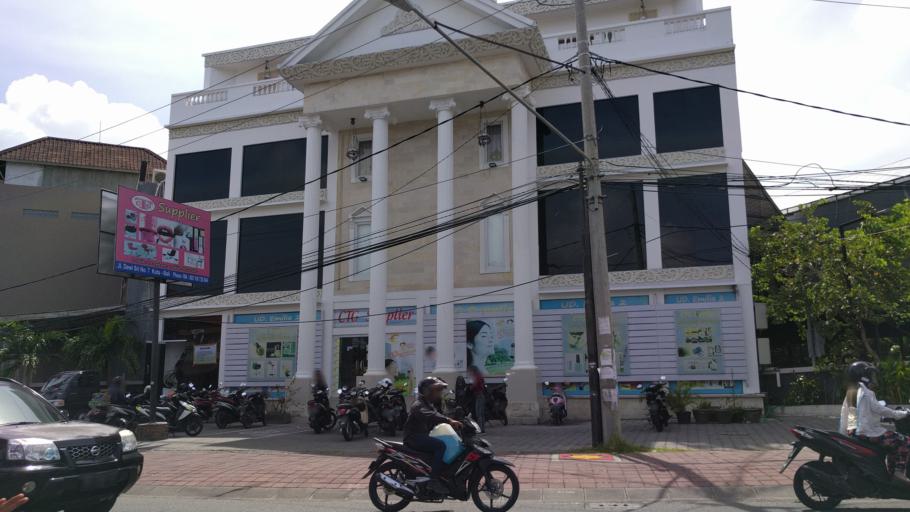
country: ID
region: Bali
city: Kuta
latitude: -8.7026
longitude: 115.1759
